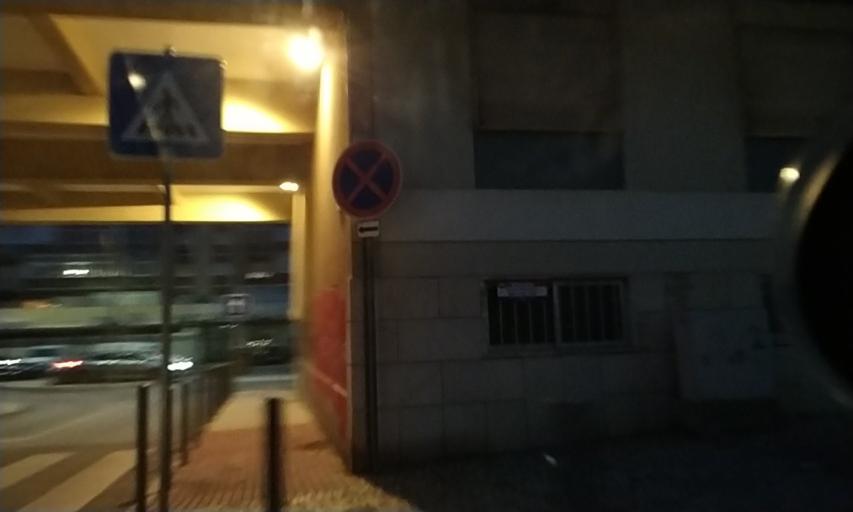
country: PT
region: Setubal
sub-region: Setubal
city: Setubal
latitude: 38.5288
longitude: -8.8938
